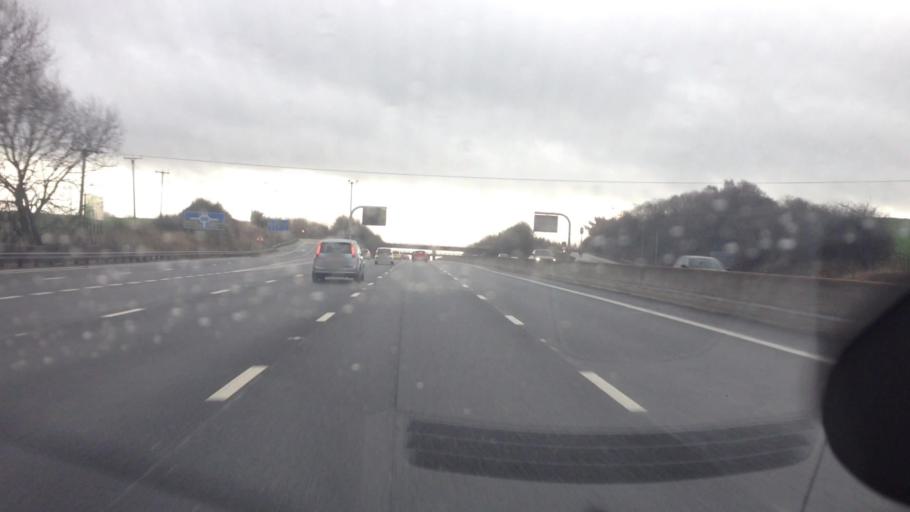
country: GB
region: England
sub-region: City and Borough of Wakefield
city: Ossett
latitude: 53.6876
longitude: -1.5560
